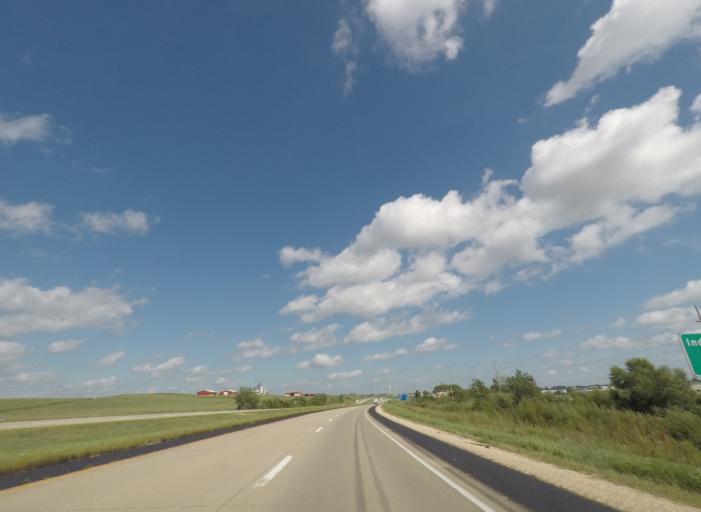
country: US
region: Iowa
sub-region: Dubuque County
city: Cascade
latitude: 42.3106
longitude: -91.0115
